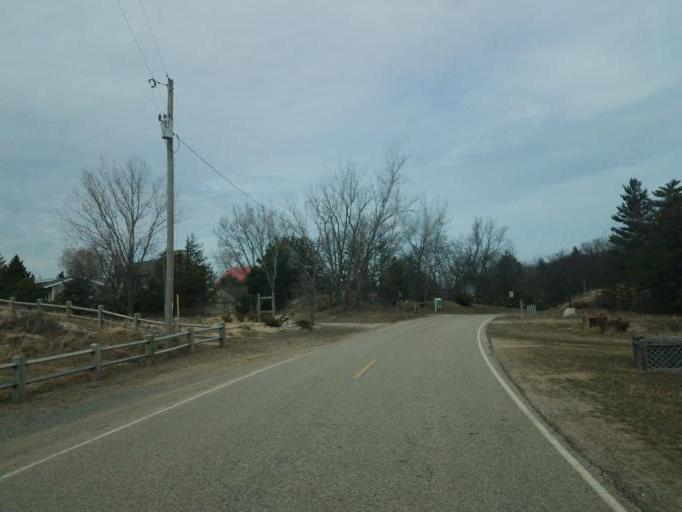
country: US
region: Michigan
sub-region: Oceana County
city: Shelby
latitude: 43.6531
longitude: -86.5381
